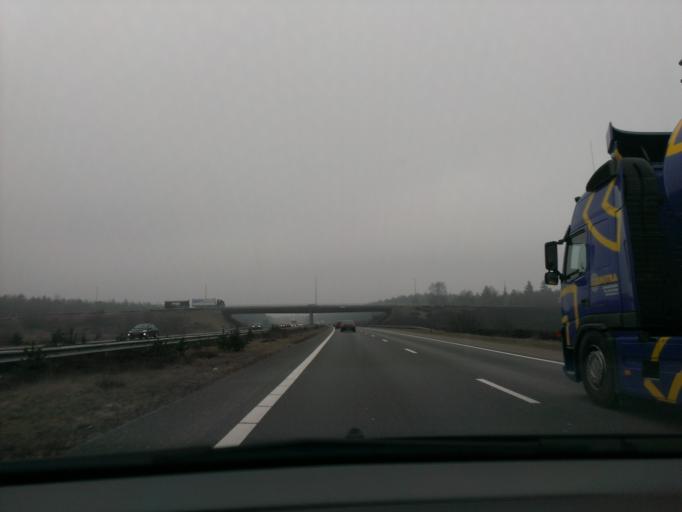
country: NL
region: Gelderland
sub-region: Gemeente Hattem
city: Hattem
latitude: 52.4624
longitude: 6.0359
